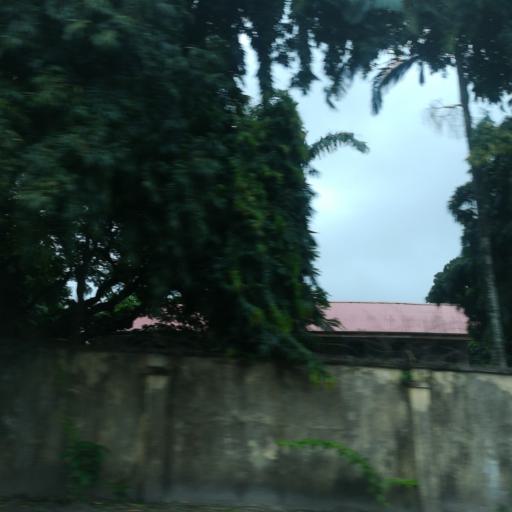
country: NG
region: Lagos
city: Ikoyi
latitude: 6.4534
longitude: 3.4479
